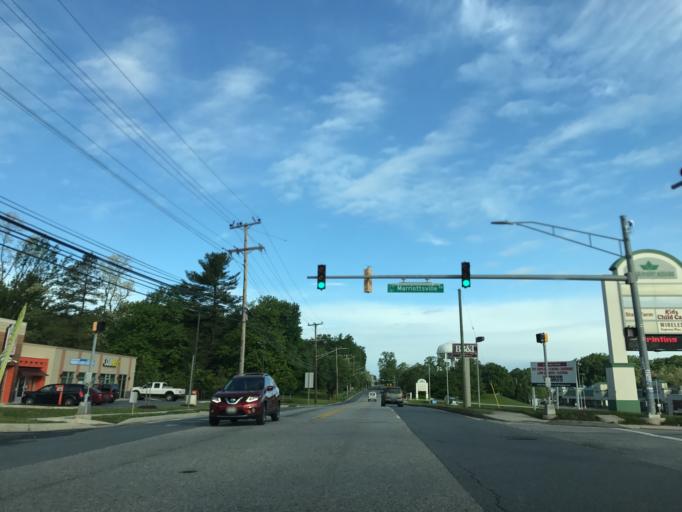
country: US
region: Maryland
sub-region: Baltimore County
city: Randallstown
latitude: 39.3812
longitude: -76.8230
